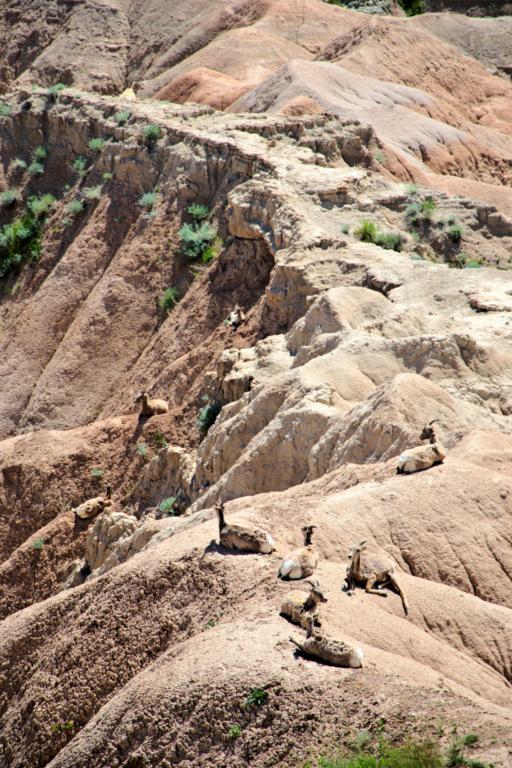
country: US
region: South Dakota
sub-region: Haakon County
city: Philip
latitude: 43.8724
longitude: -102.2525
